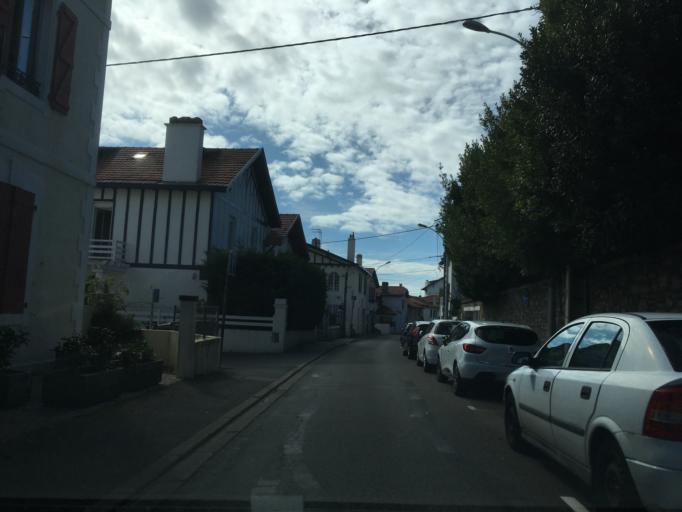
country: FR
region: Aquitaine
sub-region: Departement des Pyrenees-Atlantiques
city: Biarritz
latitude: 43.4741
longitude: -1.5601
